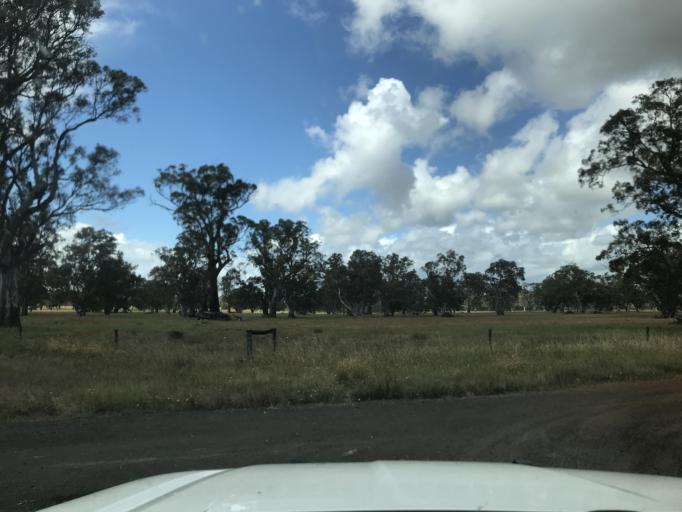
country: AU
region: South Australia
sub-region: Wattle Range
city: Penola
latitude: -37.1825
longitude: 141.4430
